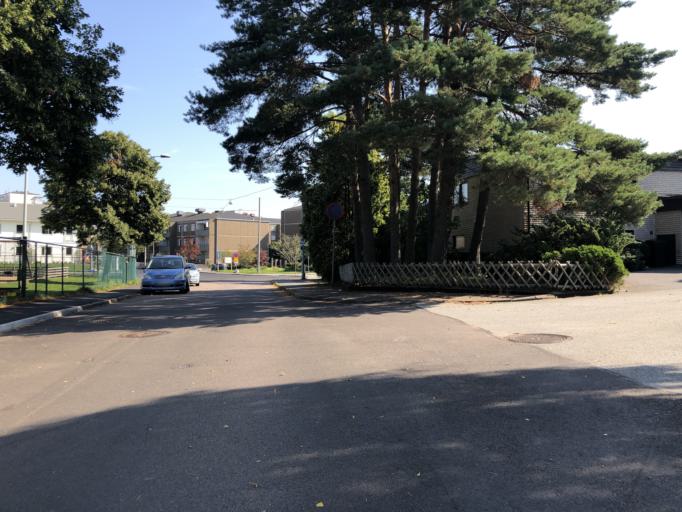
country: SE
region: Vaestra Goetaland
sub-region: Goteborg
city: Goeteborg
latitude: 57.7413
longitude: 11.9675
